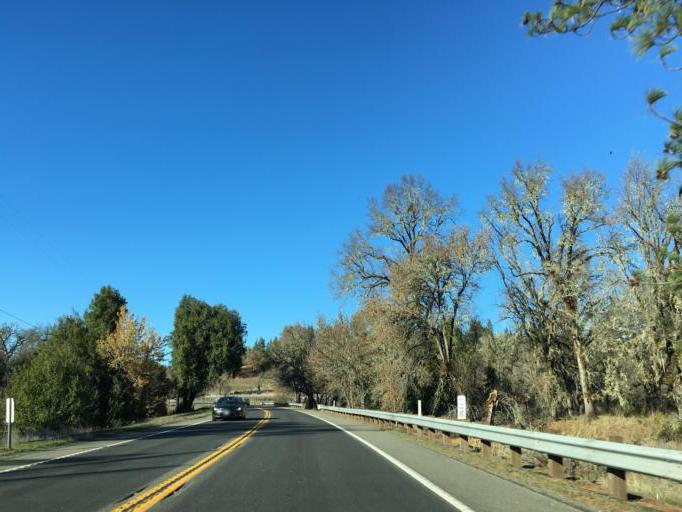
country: US
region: California
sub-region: Mendocino County
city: Laytonville
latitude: 39.7385
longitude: -123.5141
